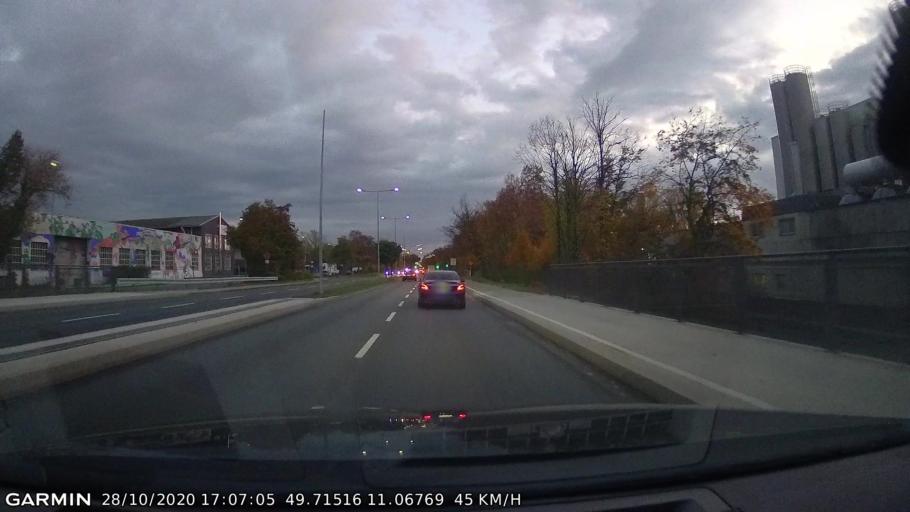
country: DE
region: Bavaria
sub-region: Upper Franconia
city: Forchheim
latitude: 49.7150
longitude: 11.0677
